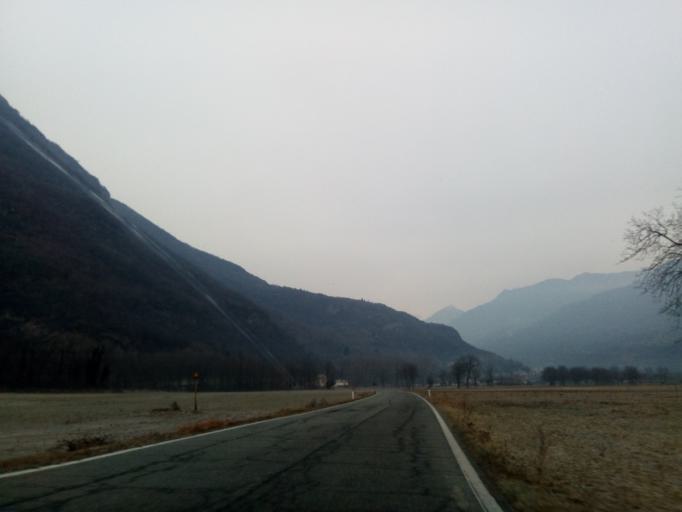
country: IT
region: Piedmont
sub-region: Provincia di Torino
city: Quassolo
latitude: 45.5120
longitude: 7.8326
